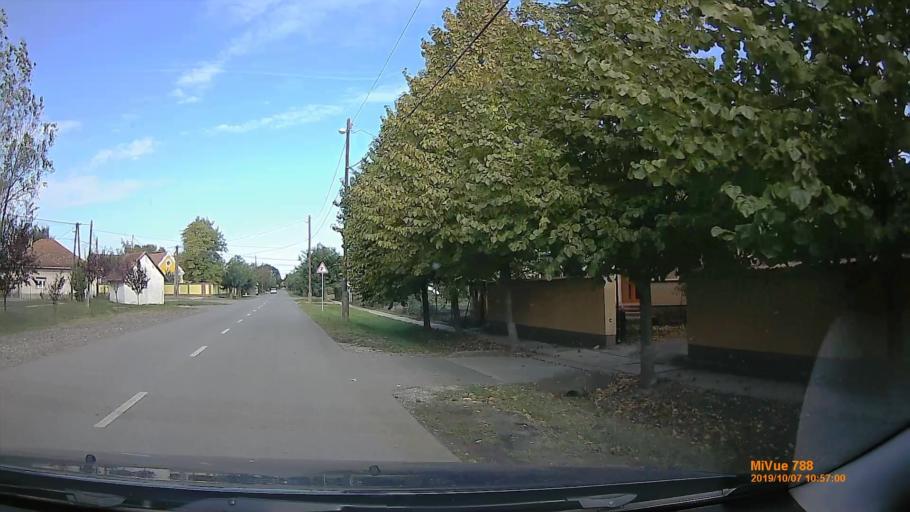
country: HU
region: Bekes
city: Kondoros
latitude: 46.7518
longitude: 20.8000
